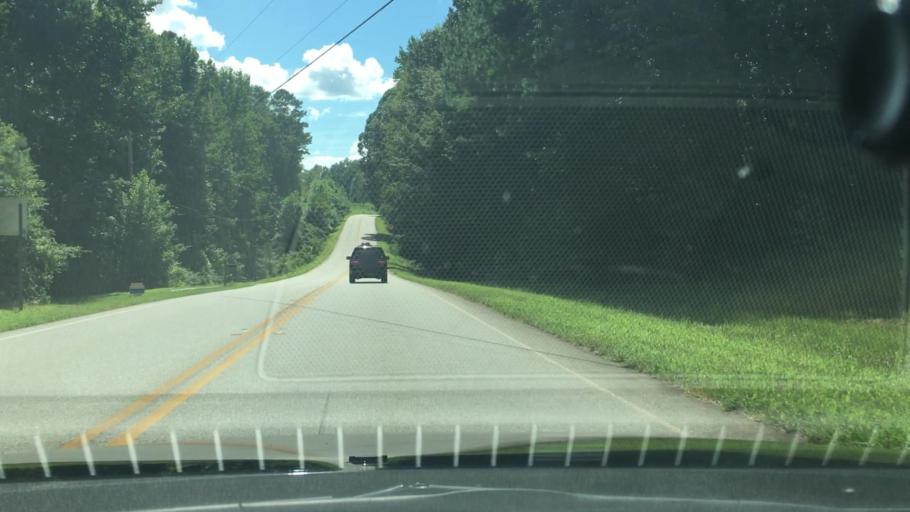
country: US
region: Georgia
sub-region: Jasper County
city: Monticello
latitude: 33.2991
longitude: -83.6659
